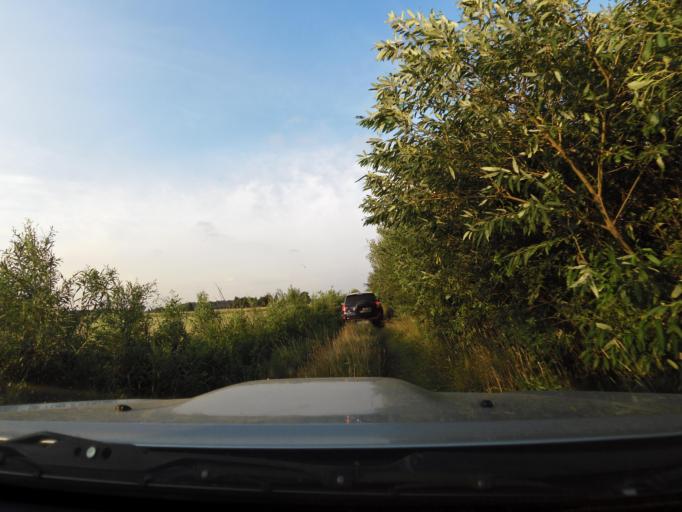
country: LT
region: Klaipedos apskritis
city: Silute
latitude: 55.4712
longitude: 21.4652
